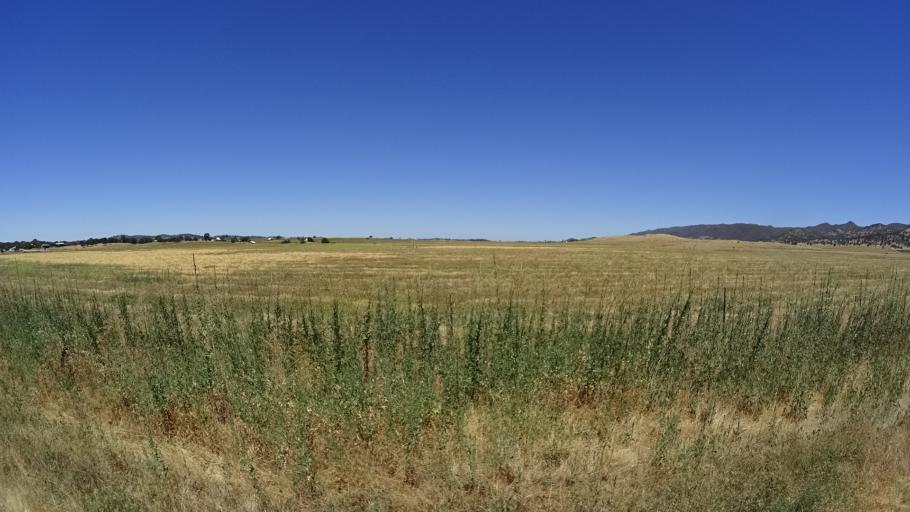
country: US
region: California
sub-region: Calaveras County
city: Copperopolis
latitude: 38.0331
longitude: -120.7111
